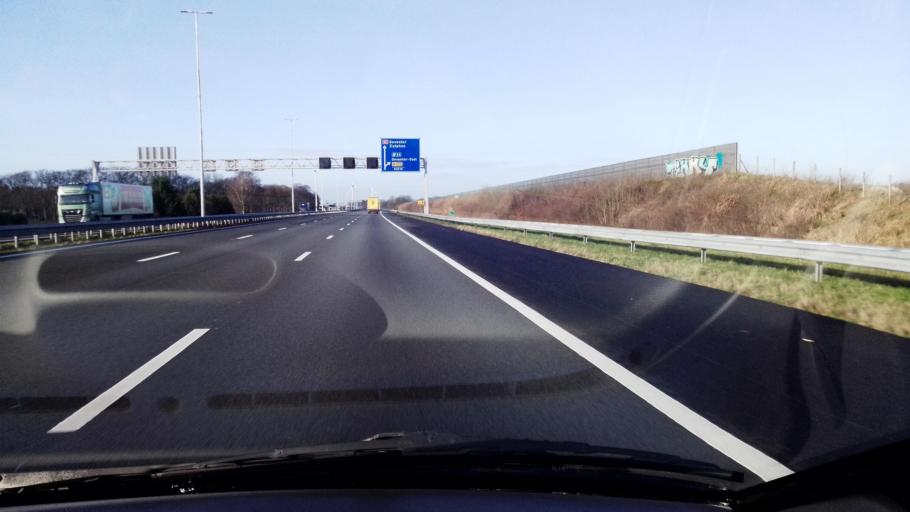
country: NL
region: Gelderland
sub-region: Gemeente Lochem
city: Epse
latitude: 52.2376
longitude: 6.2369
